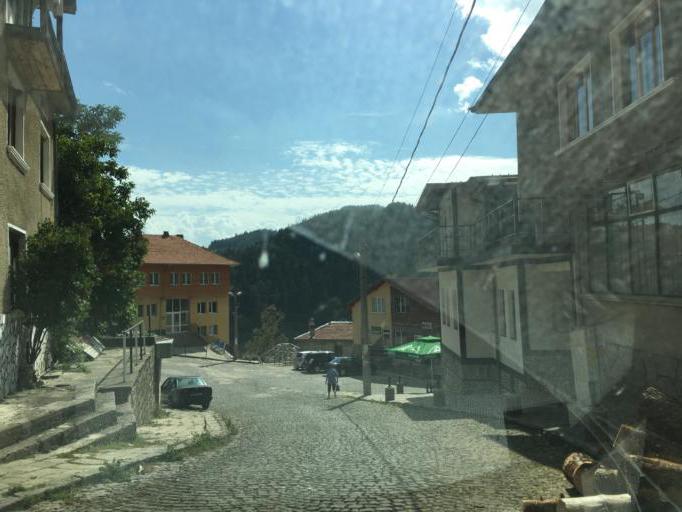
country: BG
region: Pazardzhik
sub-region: Obshtina Bratsigovo
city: Bratsigovo
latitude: 41.8836
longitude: 24.3501
